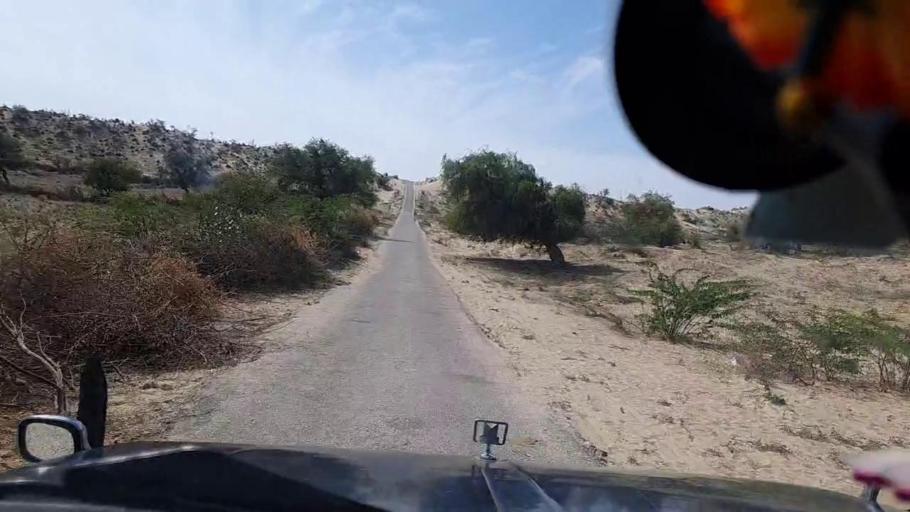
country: PK
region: Sindh
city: Diplo
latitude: 24.3972
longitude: 69.5888
